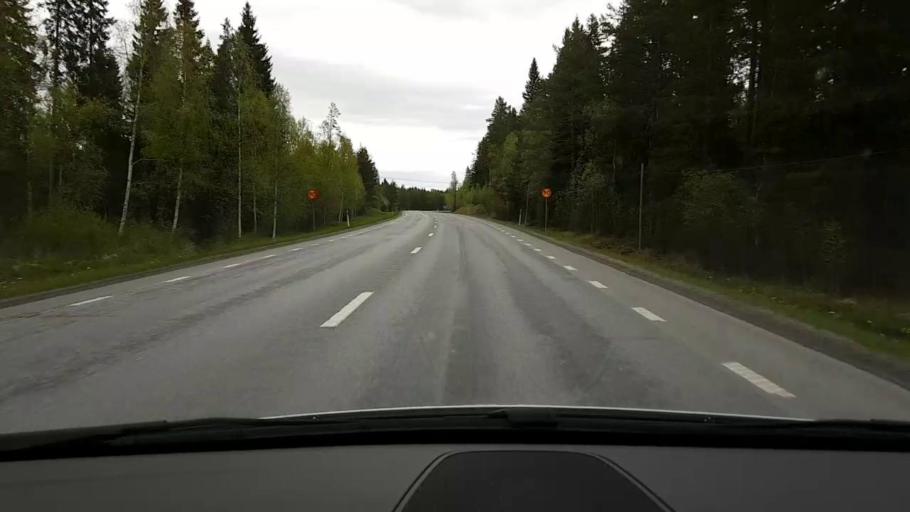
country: SE
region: Jaemtland
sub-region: Krokoms Kommun
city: Krokom
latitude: 63.3197
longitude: 14.1805
